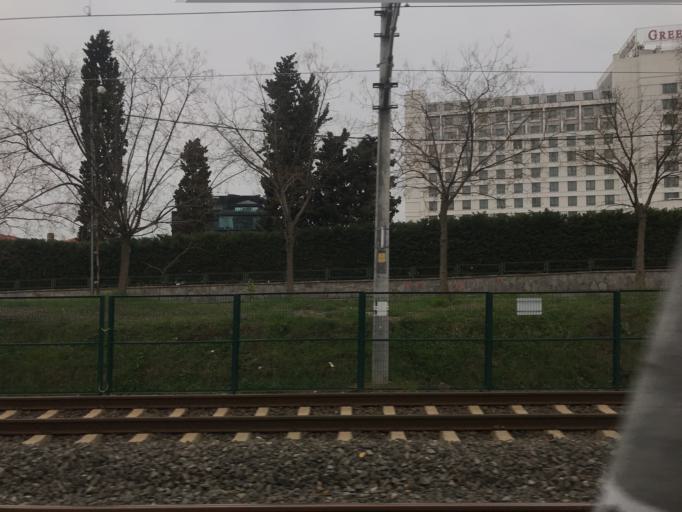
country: TR
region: Istanbul
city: Pendik
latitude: 40.8730
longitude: 29.2531
